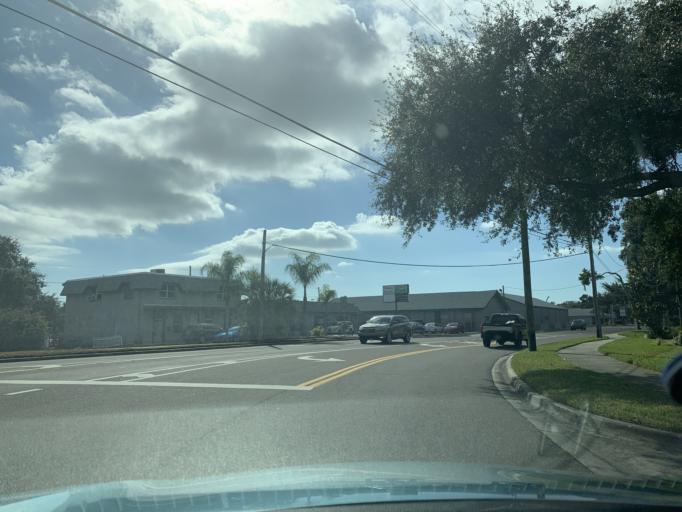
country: US
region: Florida
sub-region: Pinellas County
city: Belleair
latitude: 27.9492
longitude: -82.7959
